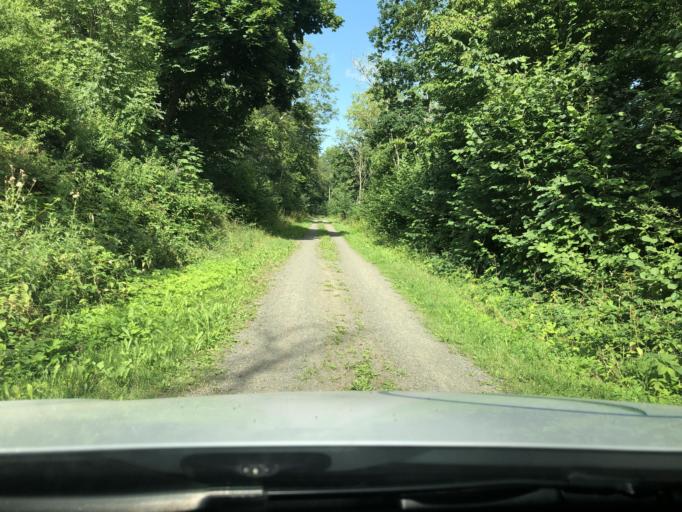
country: SE
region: Skane
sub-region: Kristianstads Kommun
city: Degeberga
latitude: 55.7751
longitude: 14.1643
